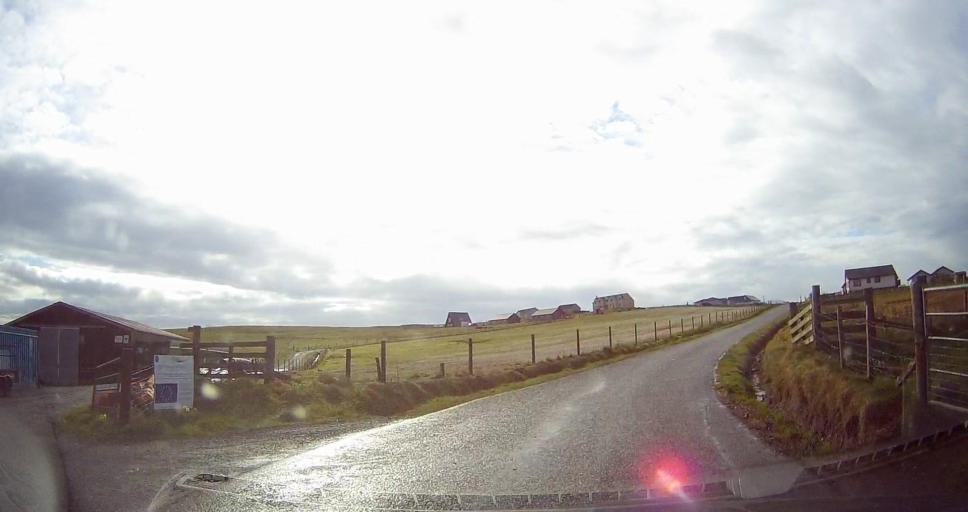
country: GB
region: Scotland
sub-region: Shetland Islands
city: Sandwick
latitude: 60.0601
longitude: -1.2162
